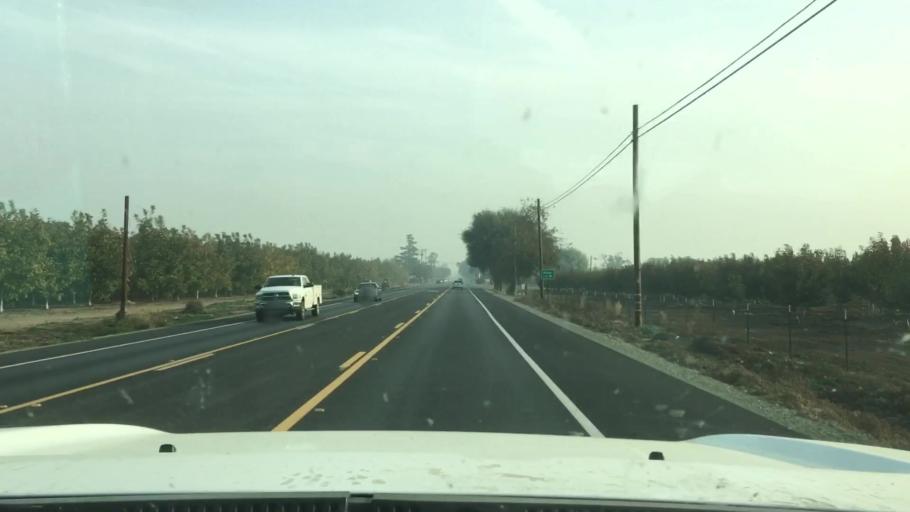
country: US
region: California
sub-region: San Joaquin County
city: August
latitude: 37.9939
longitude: -121.2358
